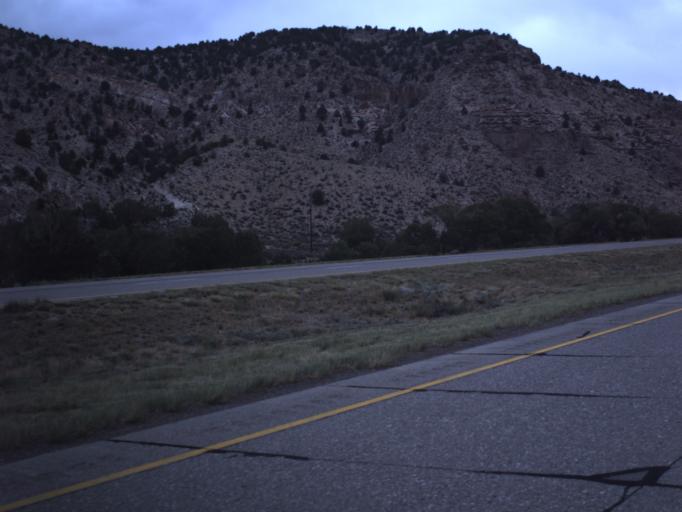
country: US
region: Utah
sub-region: Sevier County
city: Monroe
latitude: 38.5777
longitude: -112.3182
